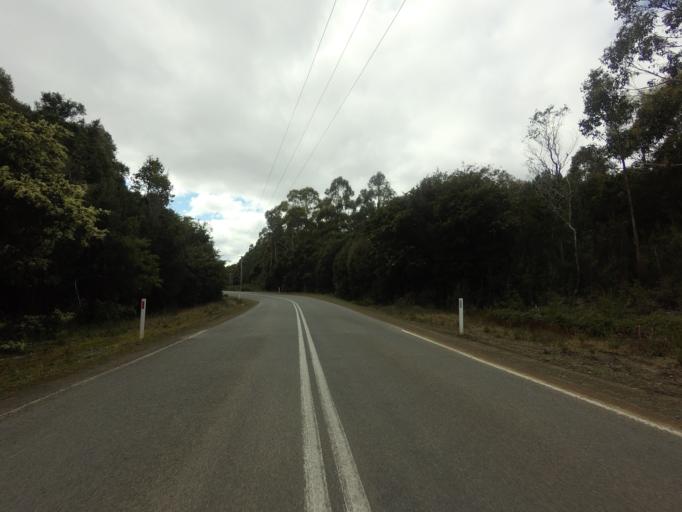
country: AU
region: Tasmania
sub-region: Huon Valley
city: Geeveston
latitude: -43.3982
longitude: 146.9562
